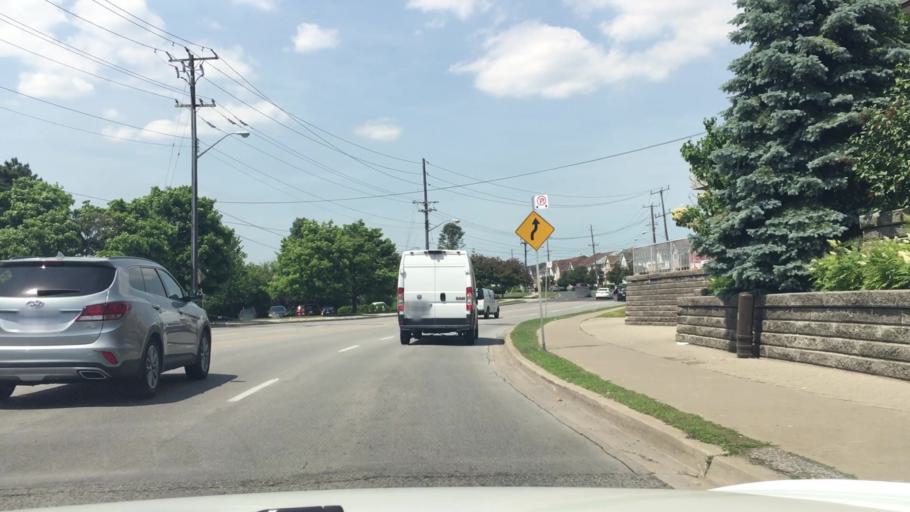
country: CA
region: Ontario
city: Scarborough
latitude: 43.7638
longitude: -79.2914
